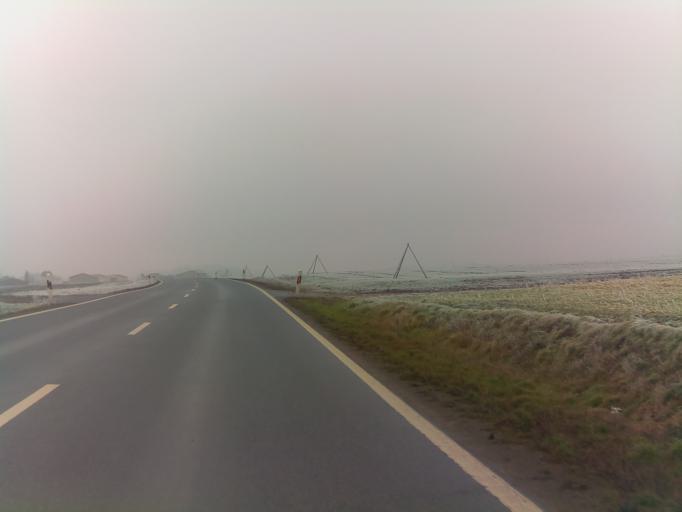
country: DE
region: Bavaria
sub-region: Regierungsbezirk Unterfranken
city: Gaukonigshofen
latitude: 49.6314
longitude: 9.9915
